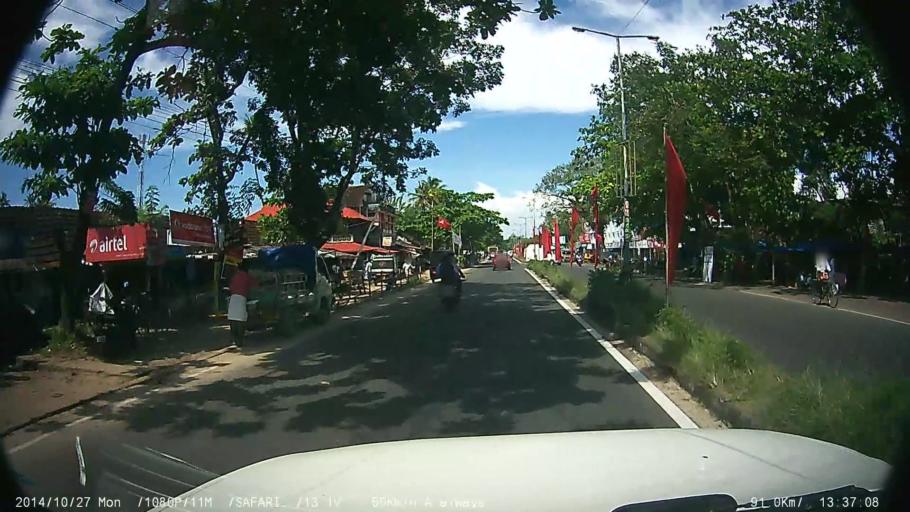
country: IN
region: Kerala
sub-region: Alappuzha
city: Shertallai
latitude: 9.6083
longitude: 76.3295
